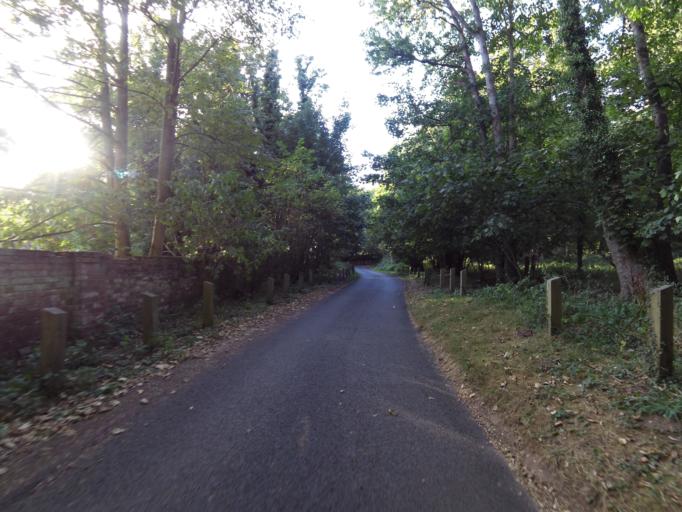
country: GB
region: England
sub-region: Suffolk
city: Kesgrave
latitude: 52.0072
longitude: 1.2329
